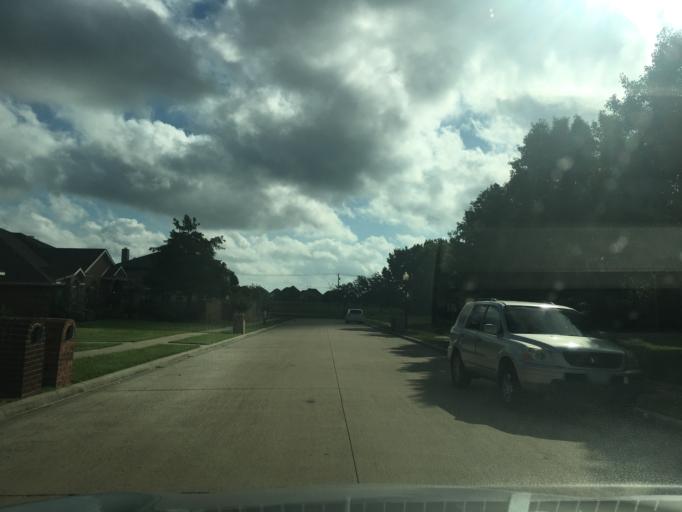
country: US
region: Texas
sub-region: Dallas County
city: Sachse
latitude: 32.9675
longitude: -96.5856
